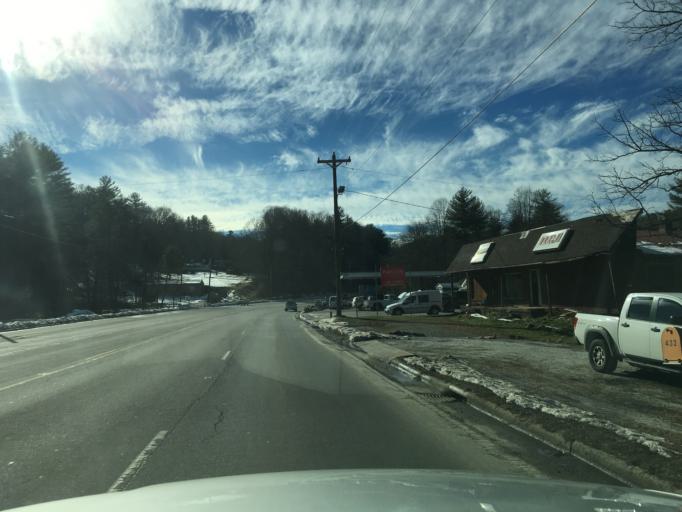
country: US
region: North Carolina
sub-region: Transylvania County
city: Brevard
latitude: 35.2225
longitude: -82.7434
